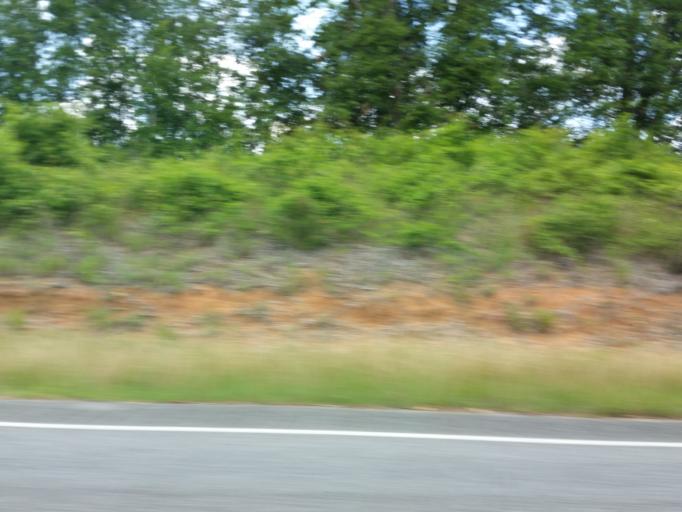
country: US
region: Alabama
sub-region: Sumter County
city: York
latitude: 32.3979
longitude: -88.2119
